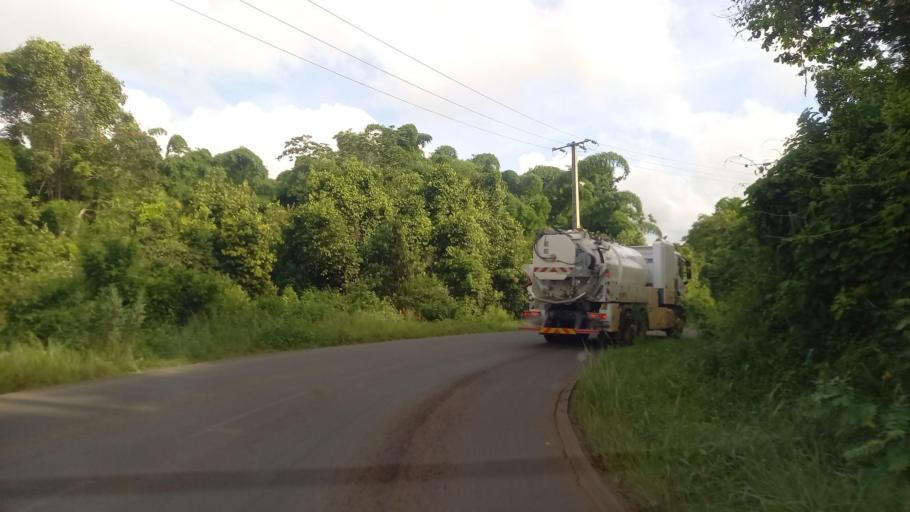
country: YT
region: Chiconi
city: Chiconi
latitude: -12.8113
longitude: 45.1260
